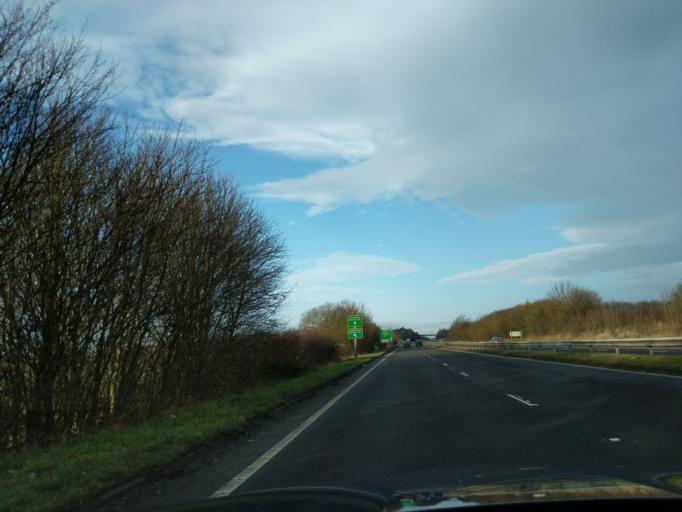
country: GB
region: England
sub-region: Newcastle upon Tyne
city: Dinnington
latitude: 55.0224
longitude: -1.7005
